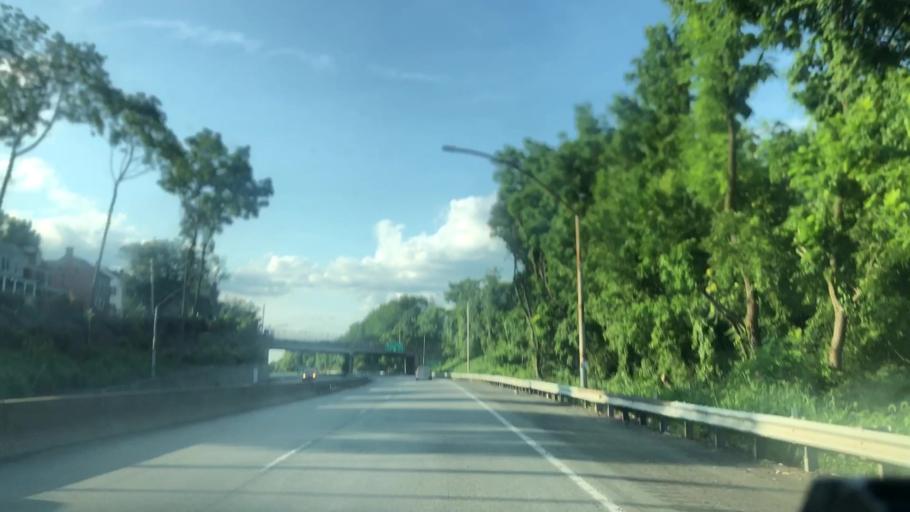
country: US
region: Pennsylvania
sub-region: Northampton County
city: Bethlehem
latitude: 40.6206
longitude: -75.3850
